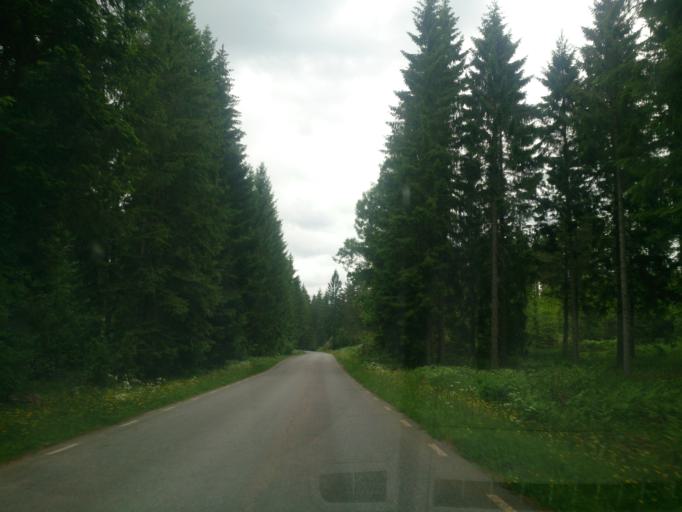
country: SE
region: OEstergoetland
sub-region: Soderkopings Kommun
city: Soederkoeping
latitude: 58.3142
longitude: 16.2867
